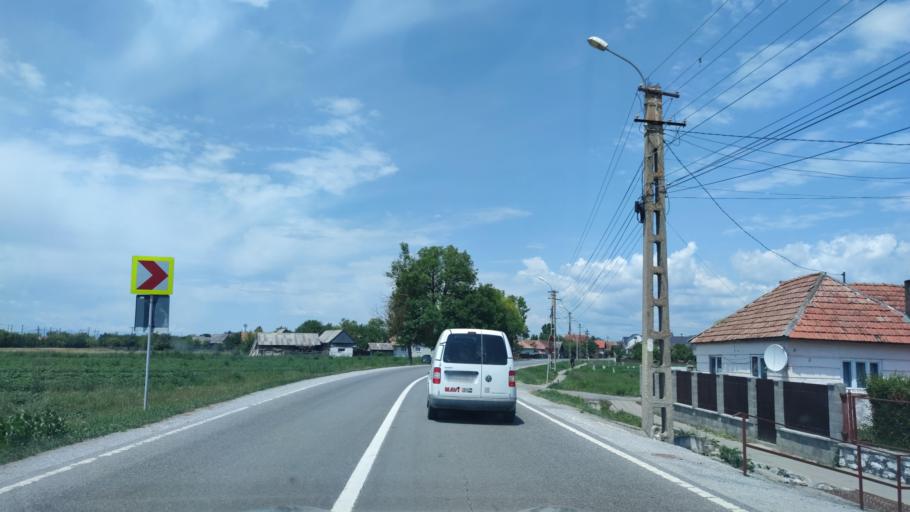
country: RO
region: Harghita
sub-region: Comuna Voslobeni
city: Voslobeni
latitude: 46.6396
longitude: 25.6249
